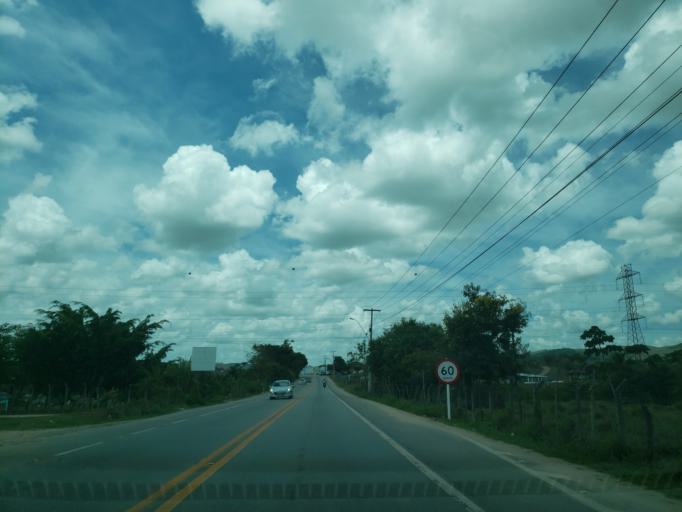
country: BR
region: Alagoas
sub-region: Uniao Dos Palmares
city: Uniao dos Palmares
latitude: -9.1606
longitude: -36.0161
